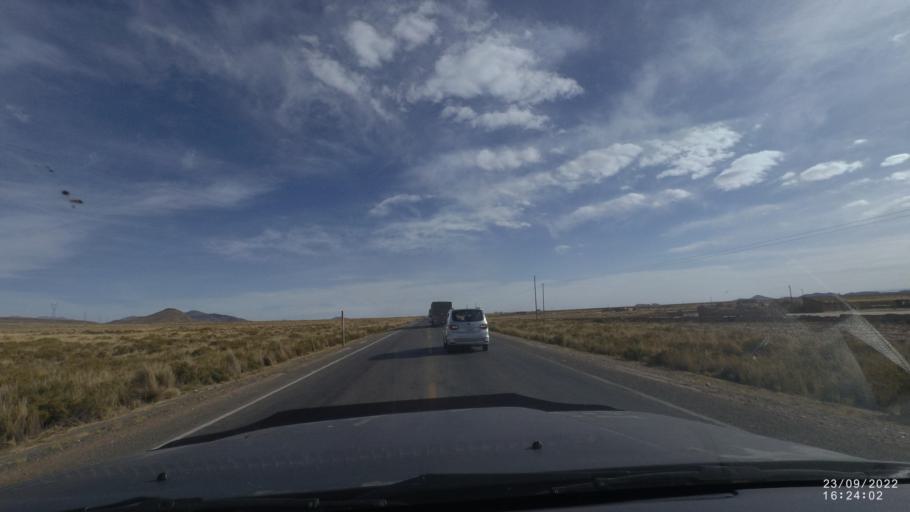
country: BO
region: Oruro
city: Machacamarca
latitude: -18.0795
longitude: -67.0069
